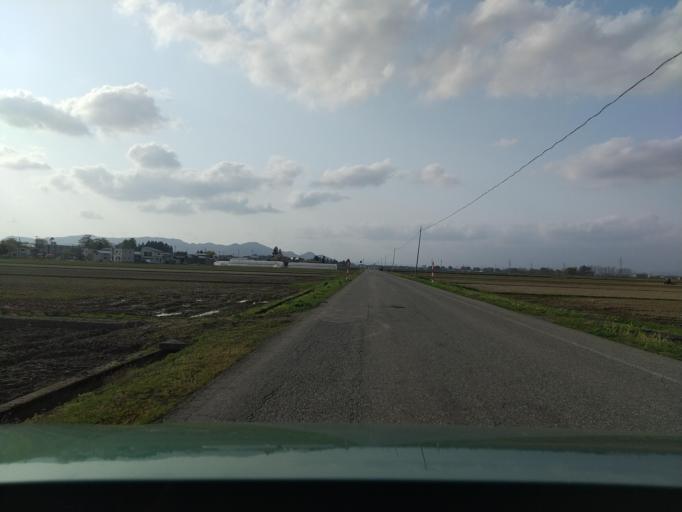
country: JP
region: Akita
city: Omagari
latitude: 39.4111
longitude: 140.4987
